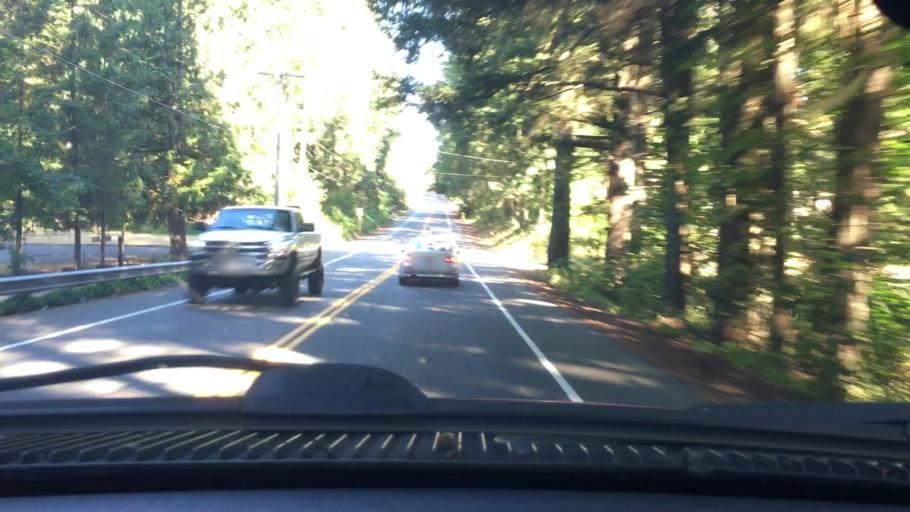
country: US
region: Washington
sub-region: King County
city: Covington
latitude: 47.3374
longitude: -122.1253
